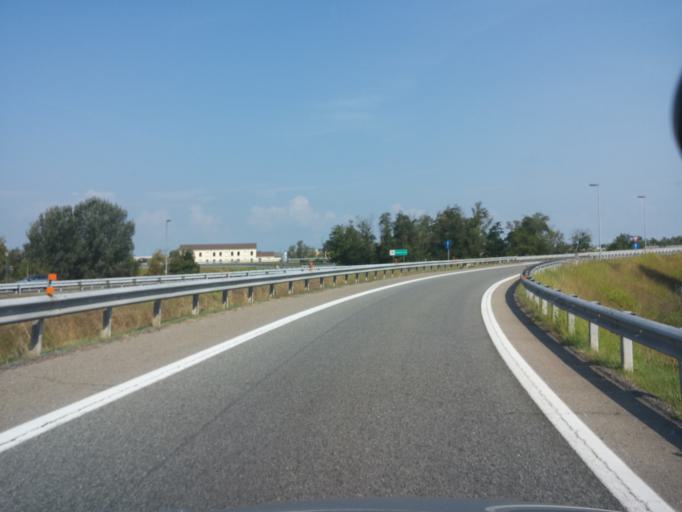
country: IT
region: Piedmont
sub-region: Provincia di Vercelli
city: Borgo Vercelli
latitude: 45.3649
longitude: 8.4858
